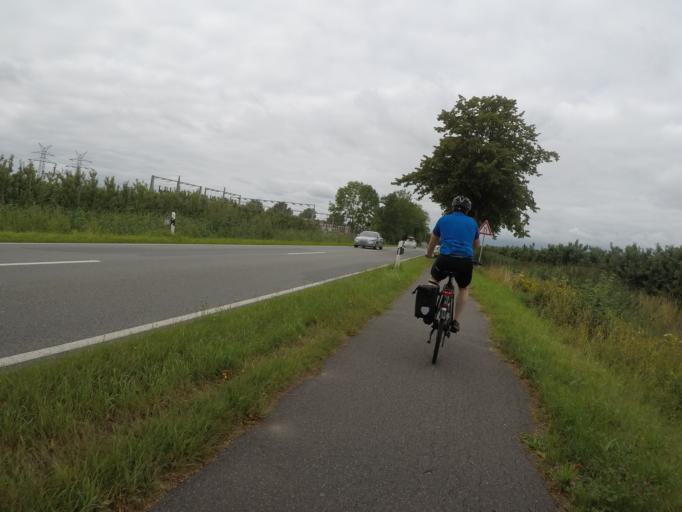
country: DE
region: Lower Saxony
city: Mittelnkirchen
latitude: 53.5394
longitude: 9.6363
